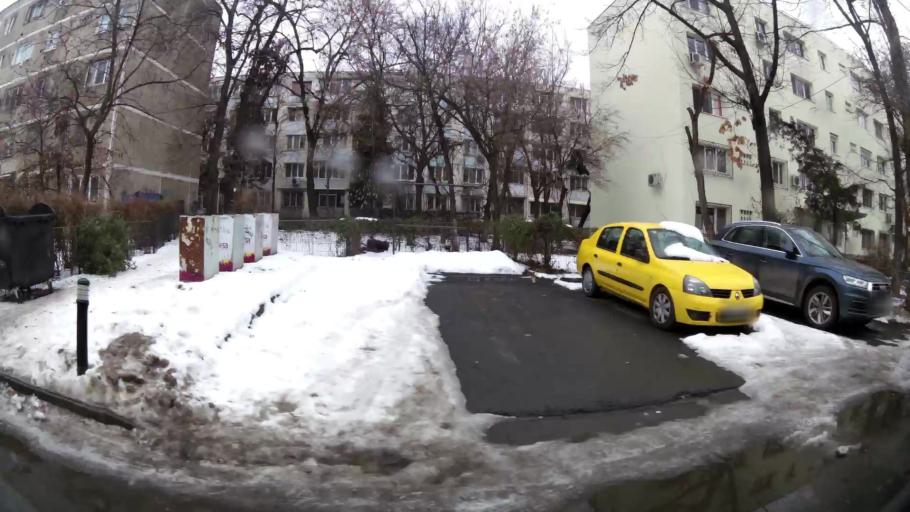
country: RO
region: Ilfov
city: Dobroesti
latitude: 44.4225
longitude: 26.1667
